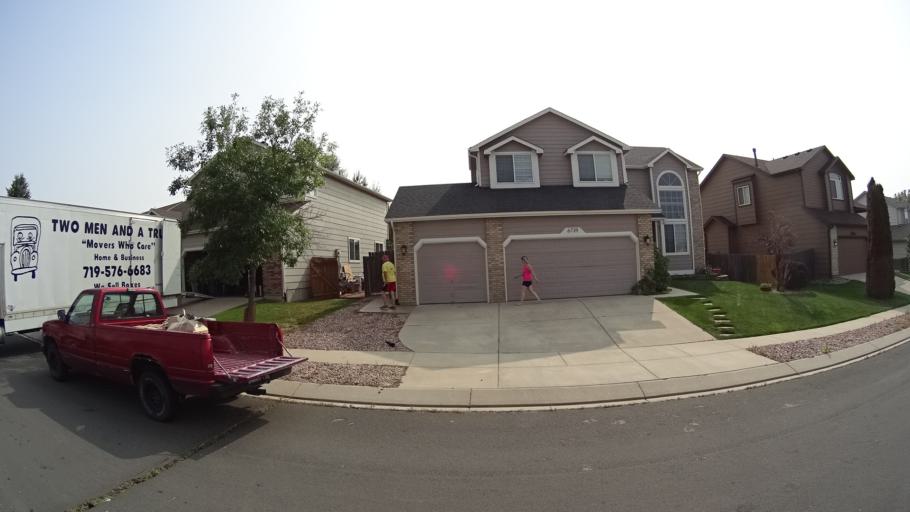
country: US
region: Colorado
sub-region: El Paso County
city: Cimarron Hills
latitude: 38.9285
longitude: -104.7369
